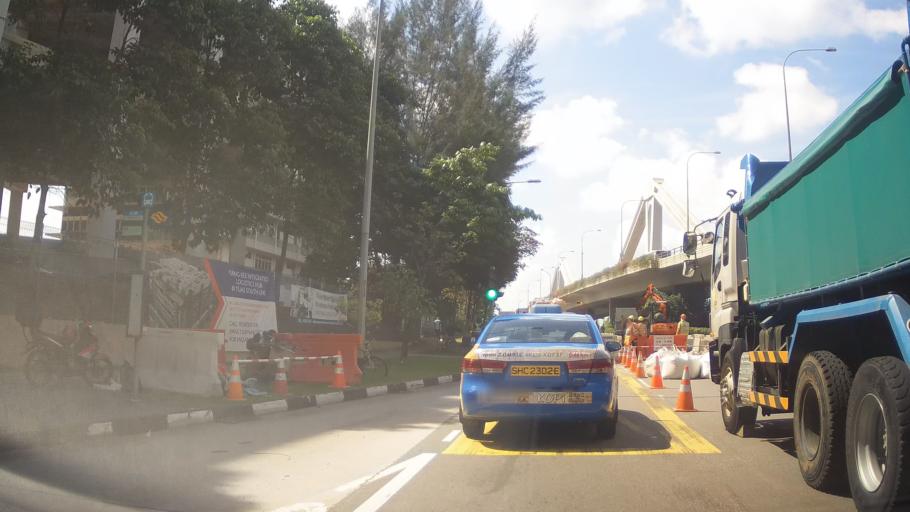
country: SG
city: Singapore
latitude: 1.3159
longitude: 103.7098
